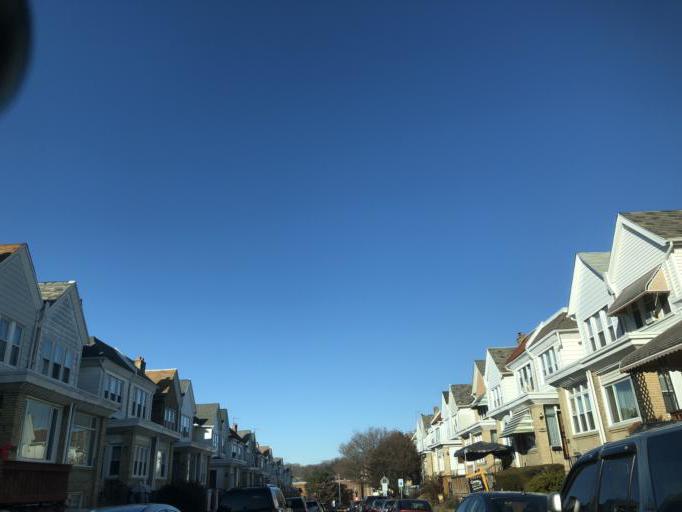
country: US
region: Pennsylvania
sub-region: Delaware County
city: East Lansdowne
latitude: 39.9554
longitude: -75.2659
